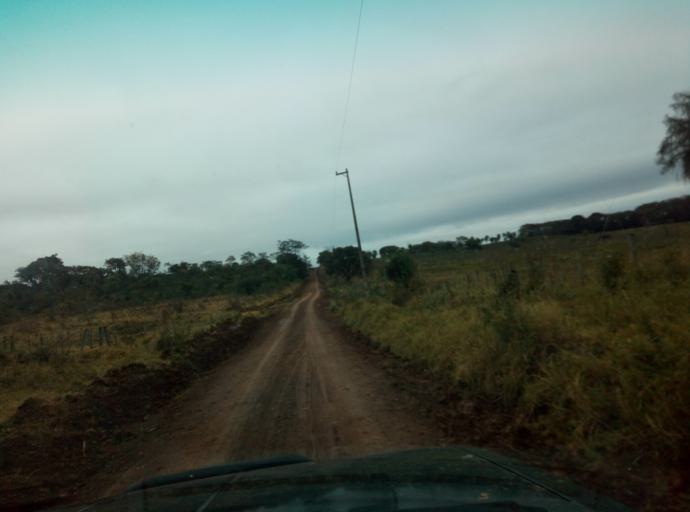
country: PY
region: Caaguazu
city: Carayao
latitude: -25.1903
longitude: -56.3715
